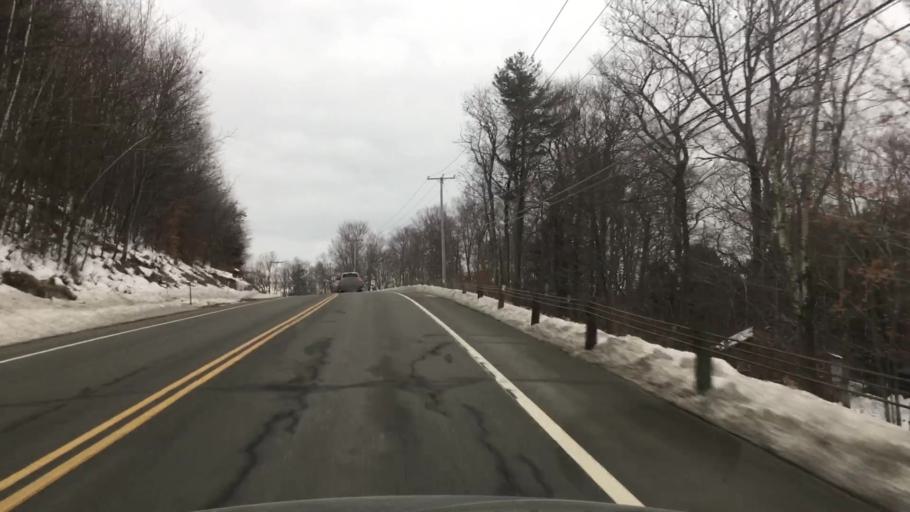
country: US
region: New Hampshire
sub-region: Merrimack County
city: Newbury
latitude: 43.3305
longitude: -72.0446
